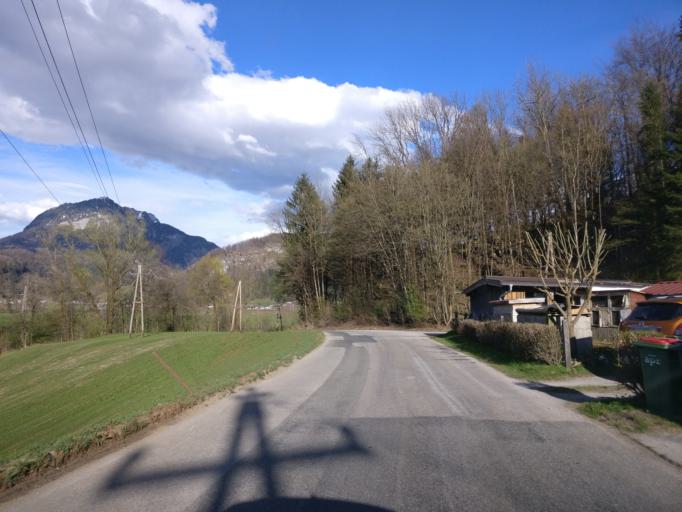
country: AT
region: Salzburg
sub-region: Politischer Bezirk Hallein
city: Golling an der Salzach
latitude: 47.5807
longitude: 13.1695
